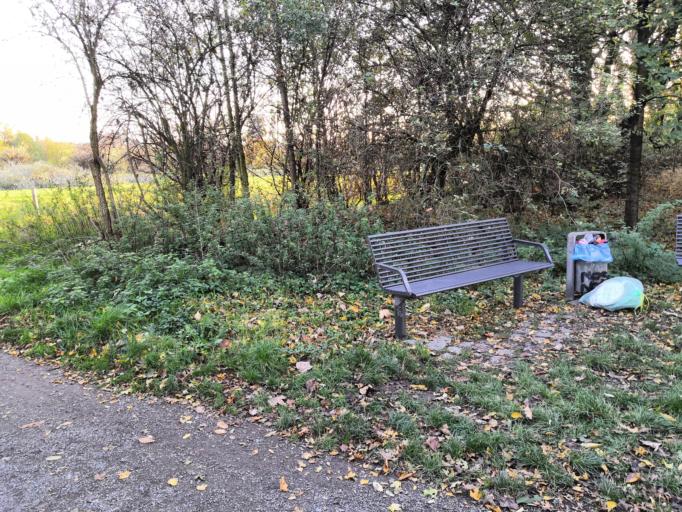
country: DE
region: North Rhine-Westphalia
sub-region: Regierungsbezirk Dusseldorf
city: Hochfeld
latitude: 51.3772
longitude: 6.7086
